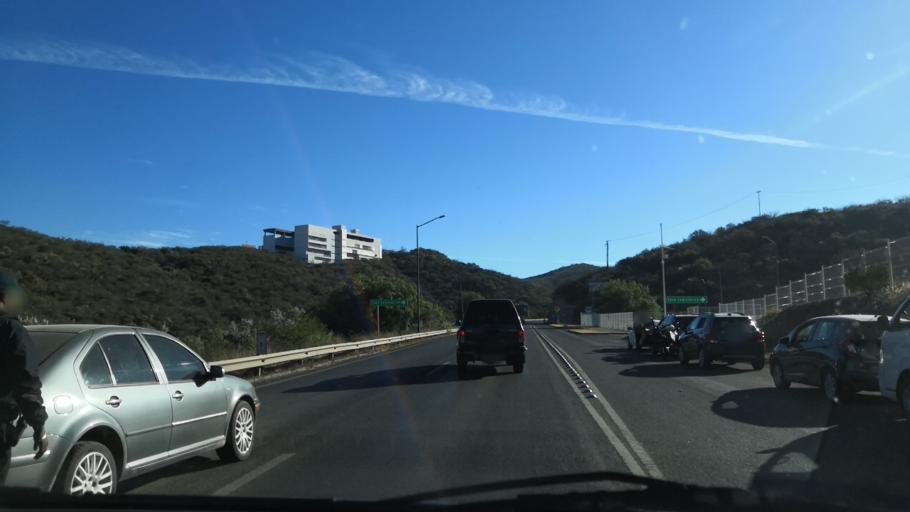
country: MX
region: Guanajuato
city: Marfil
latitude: 20.9987
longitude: -101.2770
